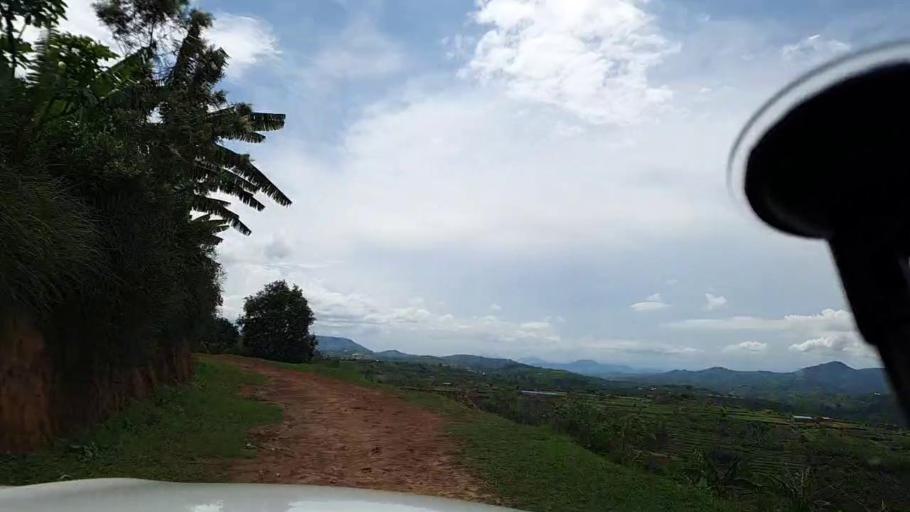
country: RW
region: Southern Province
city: Gitarama
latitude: -2.0672
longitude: 29.6443
